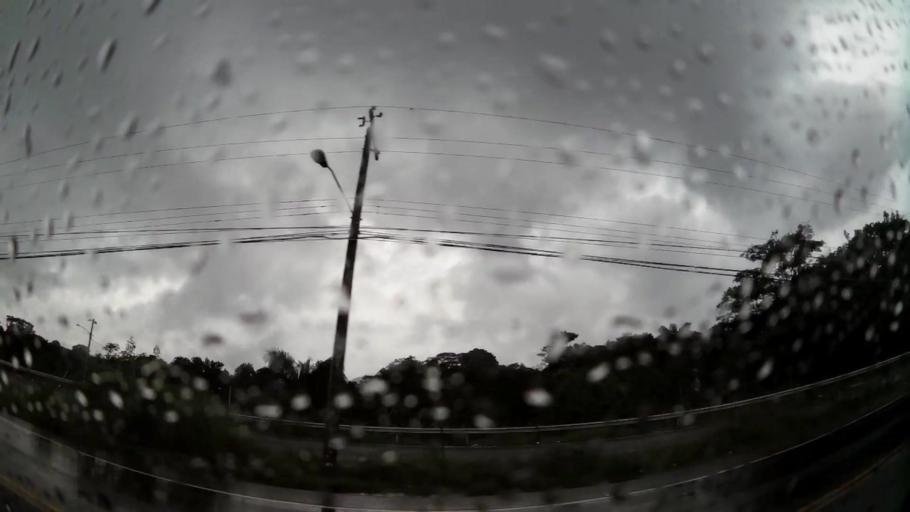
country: PA
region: Colon
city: Buena Vista
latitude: 9.2765
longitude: -79.7001
